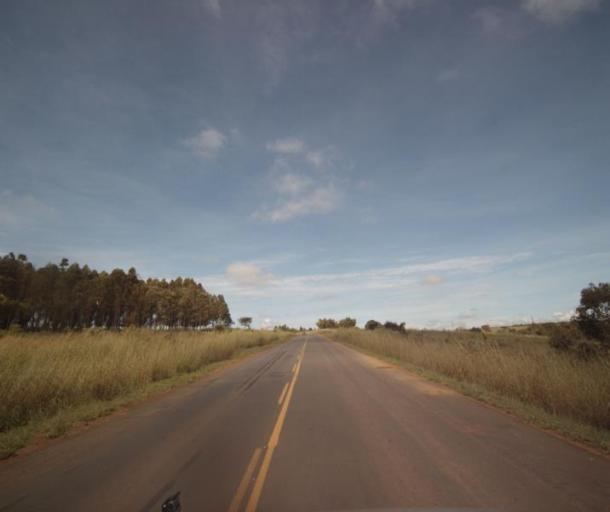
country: BR
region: Goias
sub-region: Anapolis
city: Anapolis
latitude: -16.1697
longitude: -48.8982
